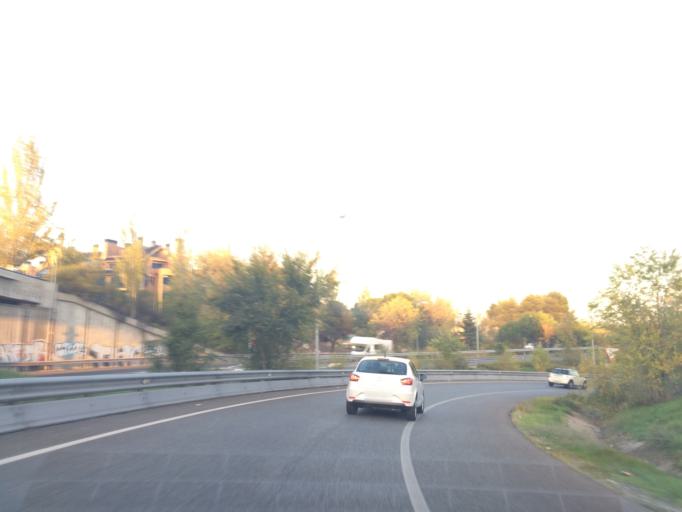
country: ES
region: Madrid
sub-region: Provincia de Madrid
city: Pozuelo de Alarcon
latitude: 40.4659
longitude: -3.7966
